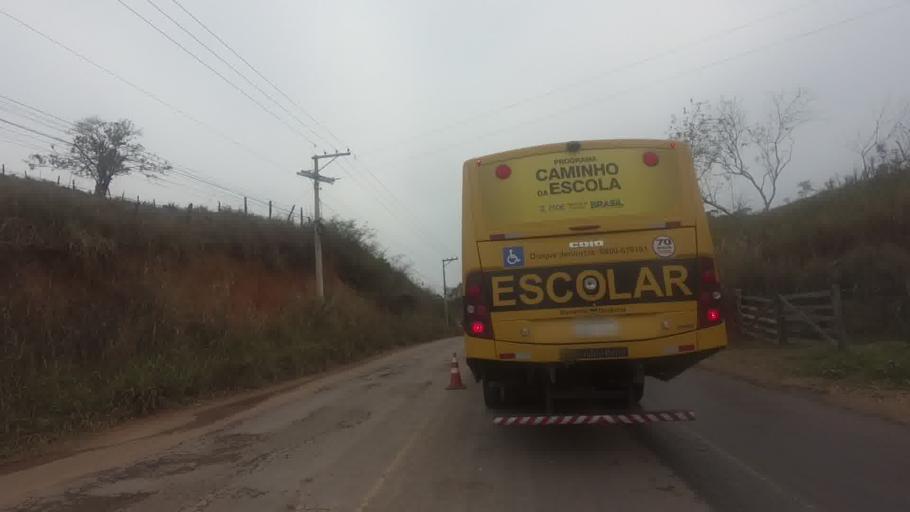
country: BR
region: Rio de Janeiro
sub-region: Santo Antonio De Padua
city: Santo Antonio de Padua
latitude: -21.6209
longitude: -42.2563
